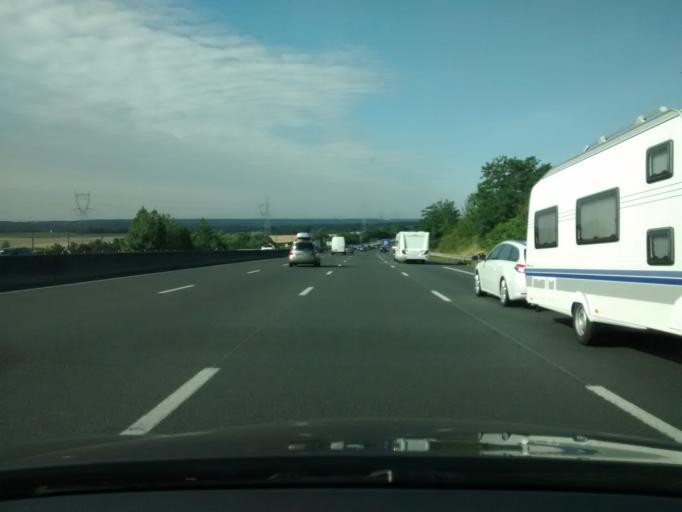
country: FR
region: Ile-de-France
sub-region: Departement de l'Essonne
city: Briis-sous-Forges
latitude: 48.6236
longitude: 2.1357
